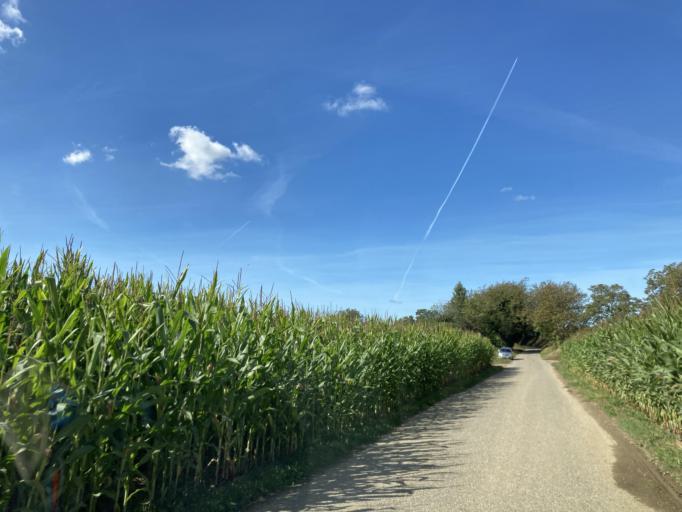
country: DE
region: Baden-Wuerttemberg
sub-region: Freiburg Region
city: Mullheim
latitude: 47.8132
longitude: 7.6466
